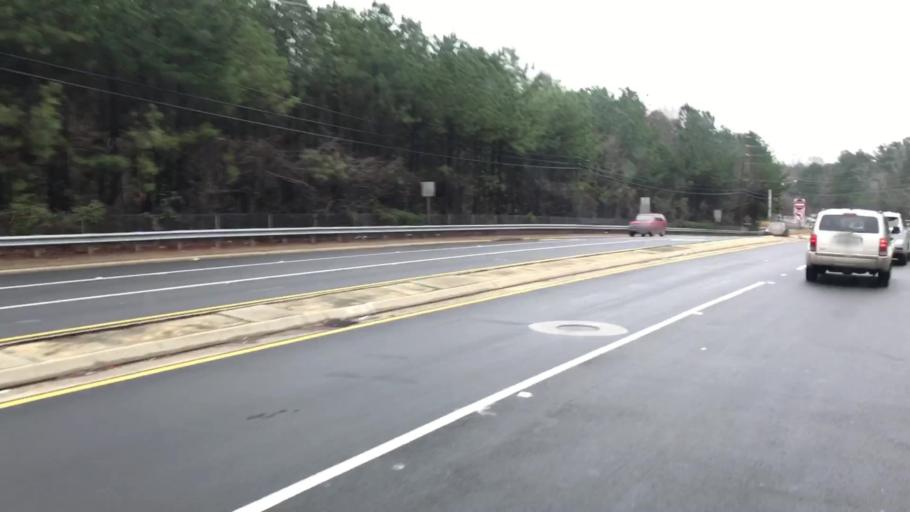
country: US
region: Georgia
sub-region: Gwinnett County
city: Snellville
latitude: 33.8525
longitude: -84.0191
